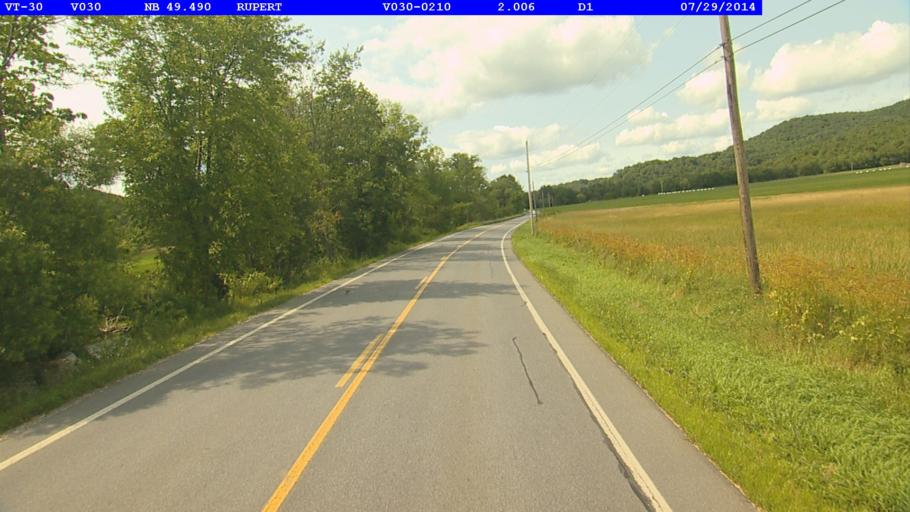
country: US
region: Vermont
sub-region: Bennington County
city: Manchester Center
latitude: 43.2951
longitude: -73.1421
